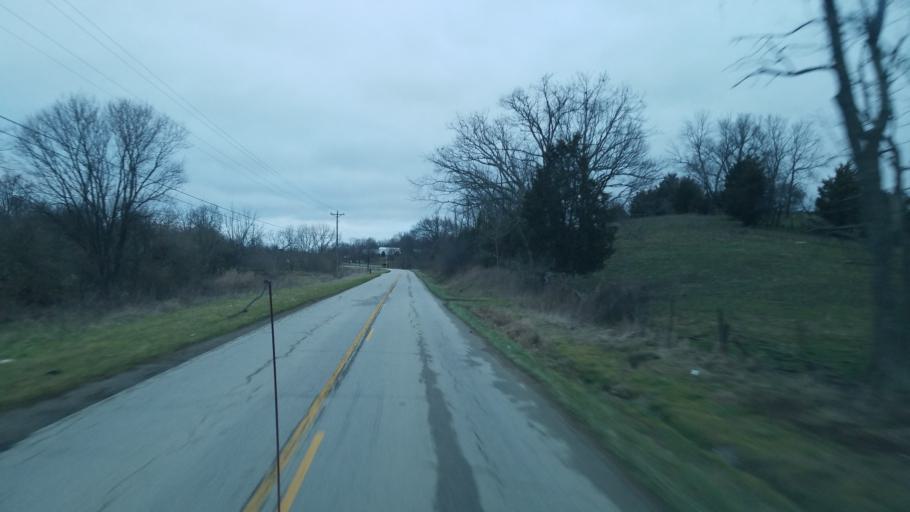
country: US
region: Kentucky
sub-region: Mason County
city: Maysville
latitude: 38.5780
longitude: -83.6971
